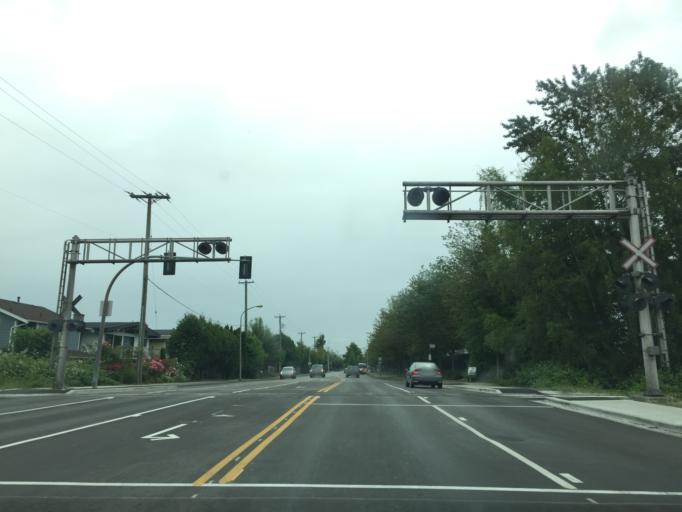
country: CA
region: British Columbia
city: Ladner
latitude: 49.1334
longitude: -123.1033
